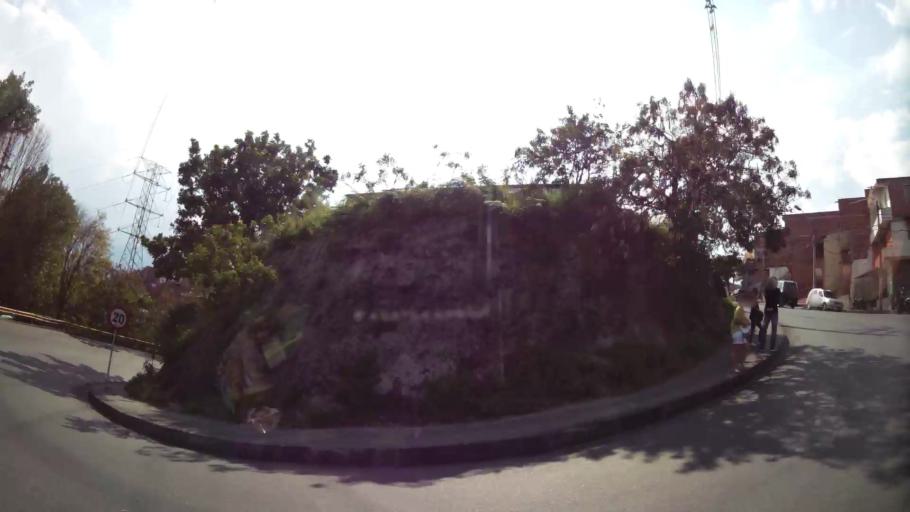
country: CO
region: Antioquia
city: Medellin
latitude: 6.2899
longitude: -75.5912
